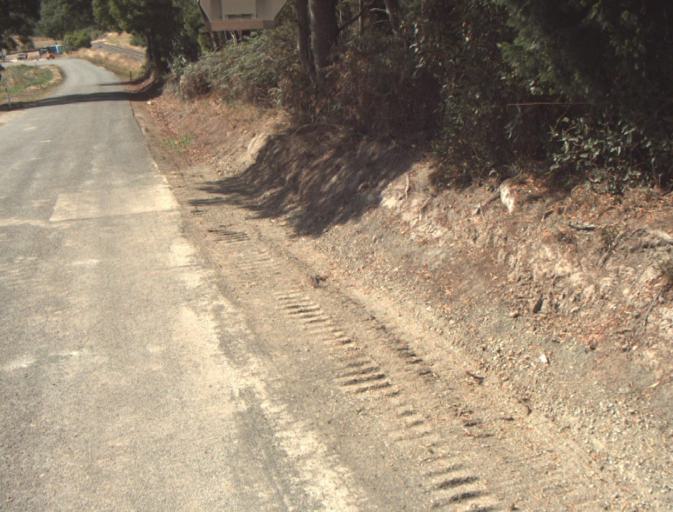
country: AU
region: Tasmania
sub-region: Launceston
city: Mayfield
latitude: -41.2594
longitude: 147.2051
